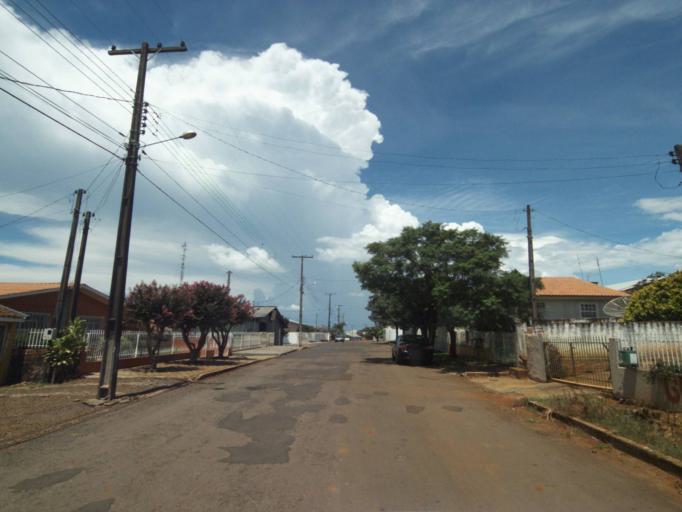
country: BR
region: Parana
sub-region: Guaraniacu
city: Guaraniacu
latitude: -25.0951
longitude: -52.8739
